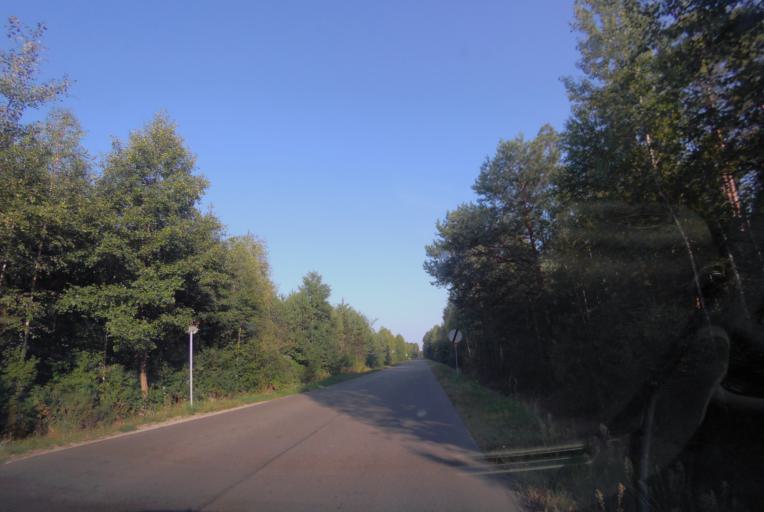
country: PL
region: Lublin Voivodeship
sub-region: Powiat bilgorajski
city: Bilgoraj
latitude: 50.5233
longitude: 22.6188
